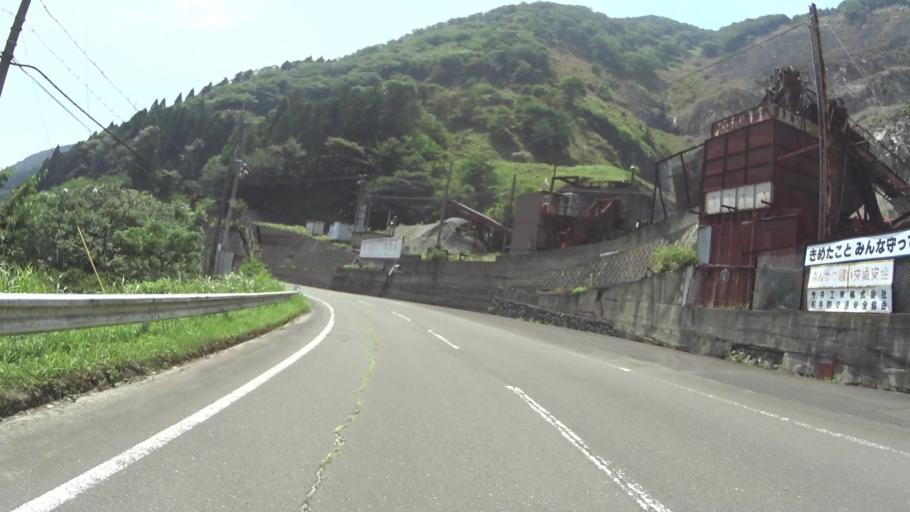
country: JP
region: Kyoto
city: Ayabe
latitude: 35.2929
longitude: 135.4263
